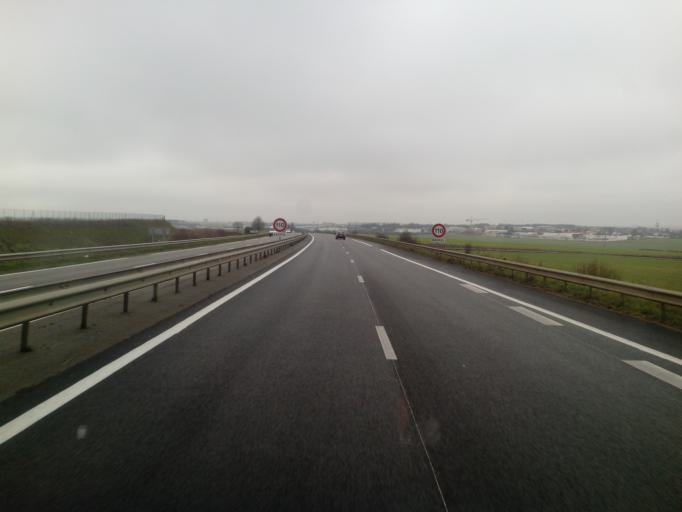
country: FR
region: Poitou-Charentes
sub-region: Departement de la Vienne
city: Migne-Auxances
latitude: 46.6192
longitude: 0.3330
